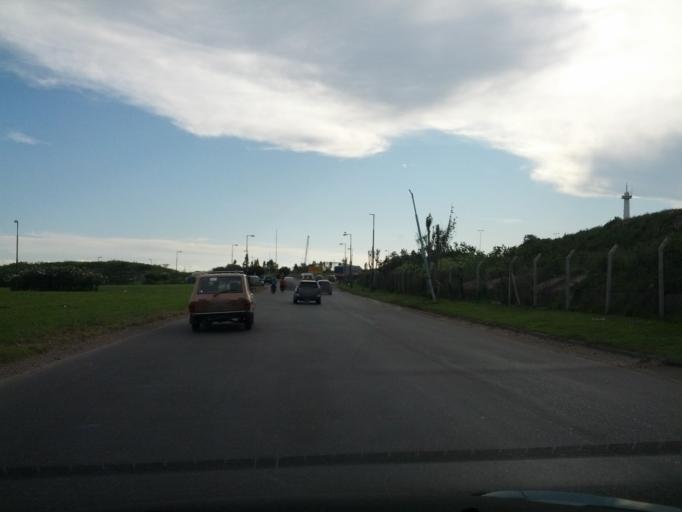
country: AR
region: Buenos Aires F.D.
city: Villa Lugano
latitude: -34.6725
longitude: -58.4341
